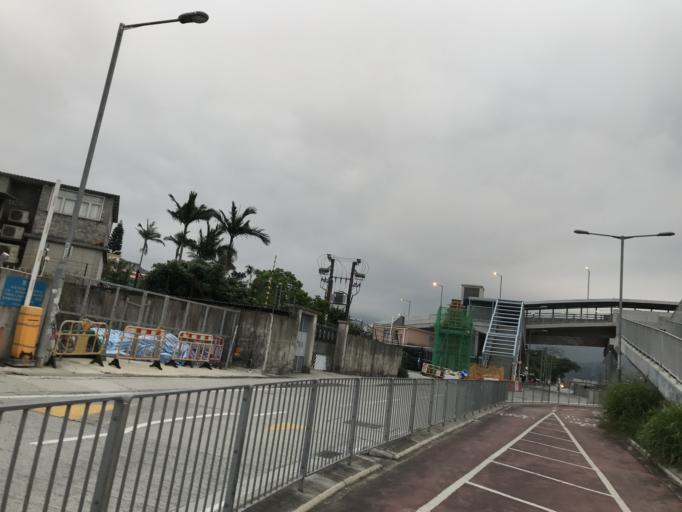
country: HK
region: Tai Po
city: Tai Po
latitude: 22.4759
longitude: 114.1546
